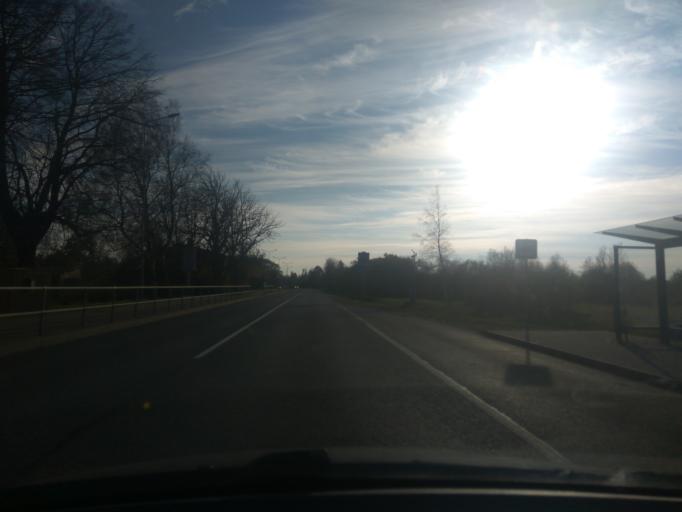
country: LV
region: Ventspils
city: Ventspils
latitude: 57.3658
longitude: 21.5639
